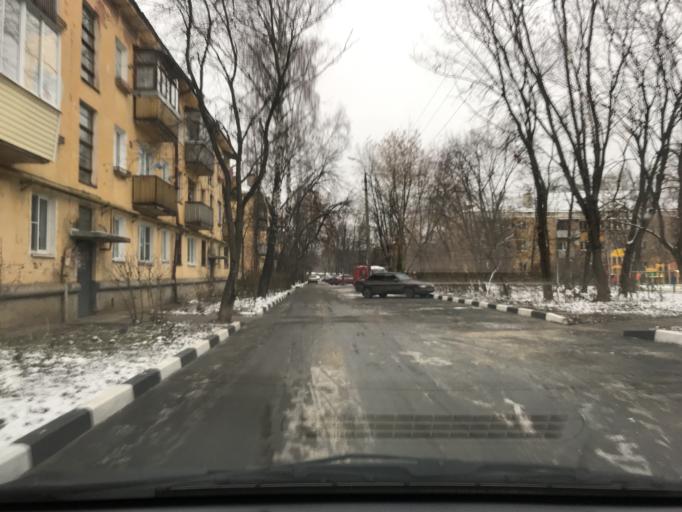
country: RU
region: Moskovskaya
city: Elektrostal'
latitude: 55.8054
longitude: 38.4621
